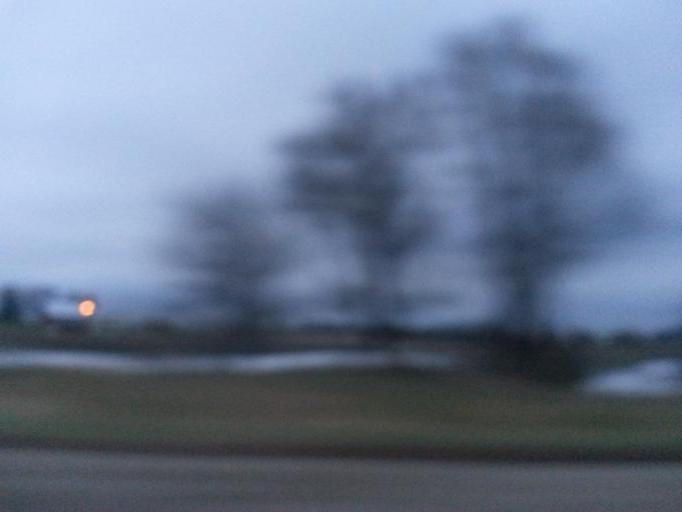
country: US
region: Iowa
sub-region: Black Hawk County
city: Elk Run Heights
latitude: 42.4206
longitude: -92.1818
